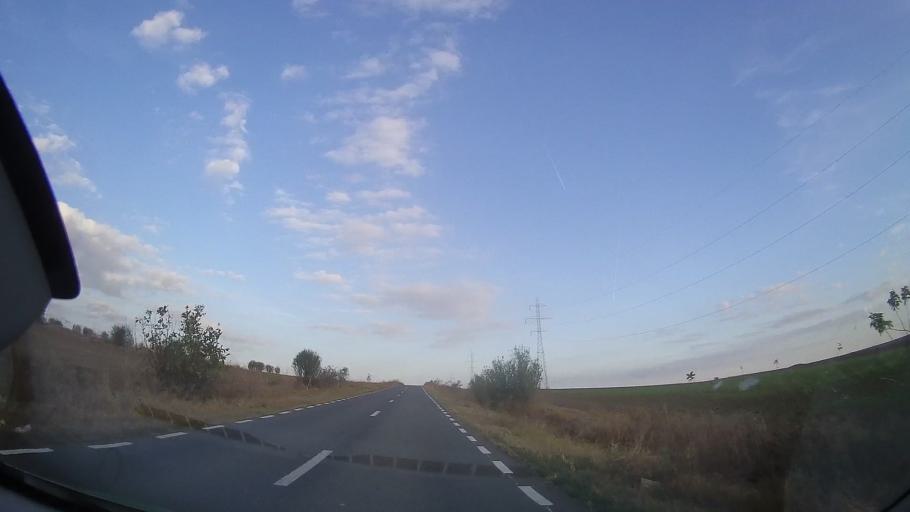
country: RO
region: Constanta
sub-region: Comuna Chirnogeni
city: Plopeni
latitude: 43.9520
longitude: 28.1635
